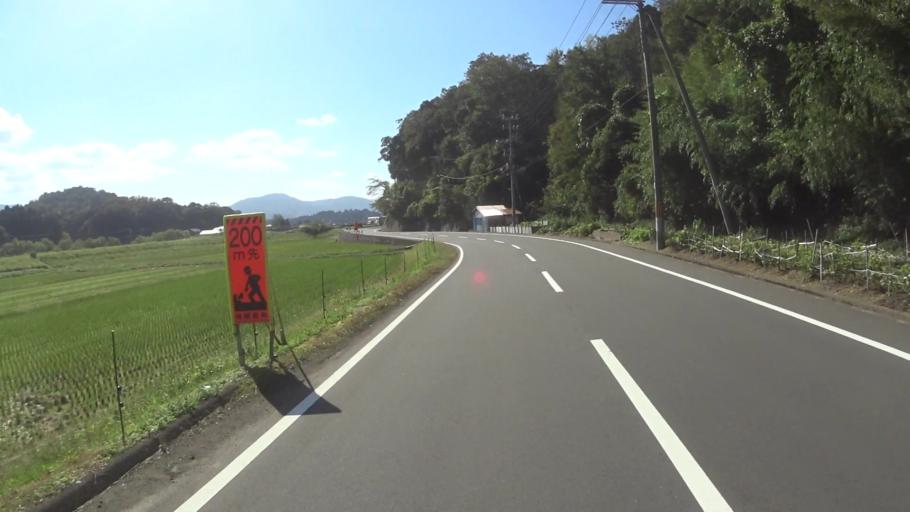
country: JP
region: Kyoto
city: Miyazu
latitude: 35.6916
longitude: 135.0967
